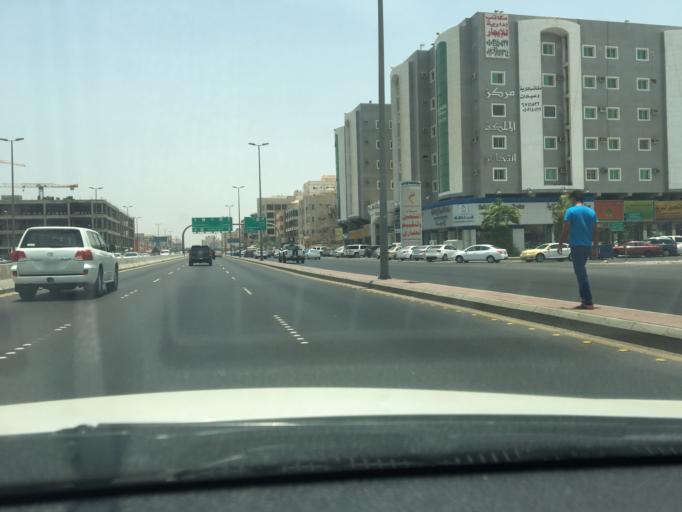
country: SA
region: Makkah
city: Jeddah
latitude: 21.5534
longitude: 39.1886
